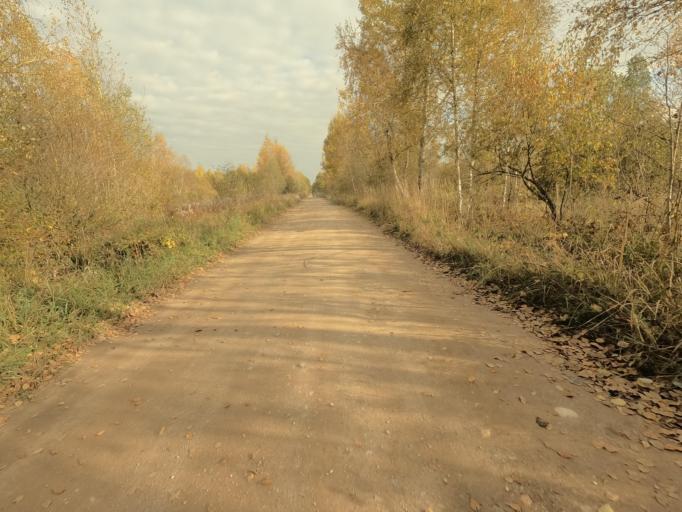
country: RU
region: Novgorod
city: Pankovka
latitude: 58.8949
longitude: 31.0126
